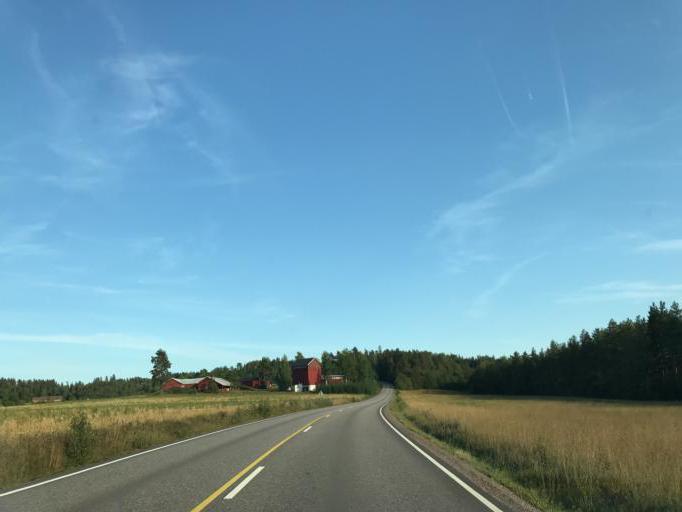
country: FI
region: Uusimaa
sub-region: Helsinki
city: Vihti
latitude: 60.4223
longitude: 24.3648
